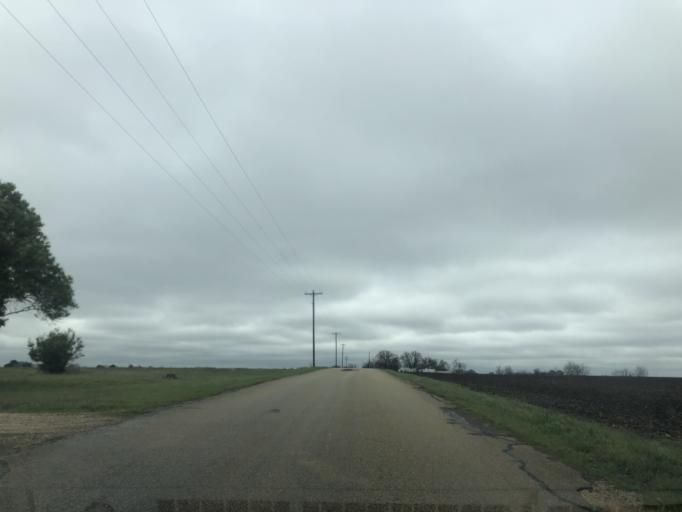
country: US
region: Texas
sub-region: Williamson County
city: Hutto
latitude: 30.5789
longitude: -97.4952
